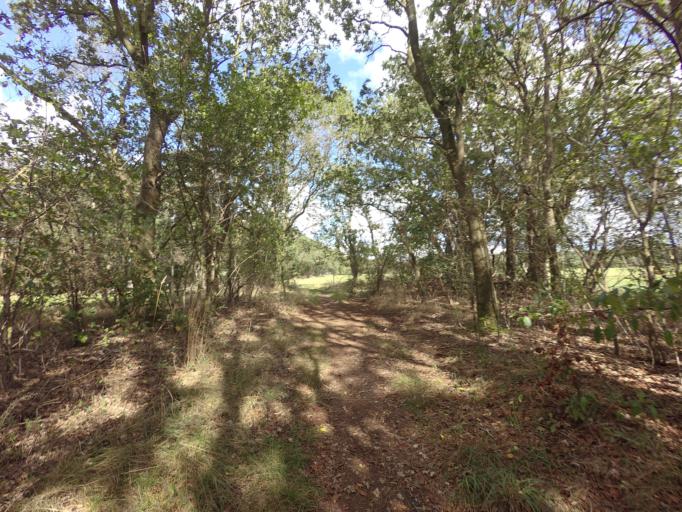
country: NL
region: Friesland
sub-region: Gemeente Weststellingwerf
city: Noordwolde
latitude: 52.9559
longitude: 6.2014
